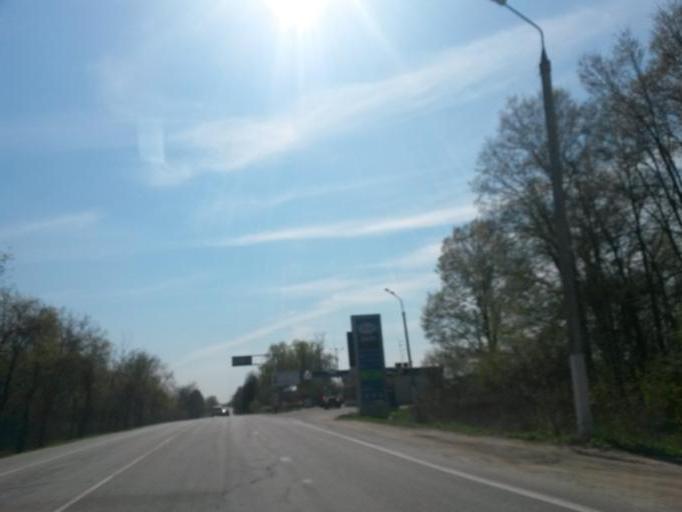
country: RU
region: Moskovskaya
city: L'vovskiy
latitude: 55.2917
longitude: 37.5185
